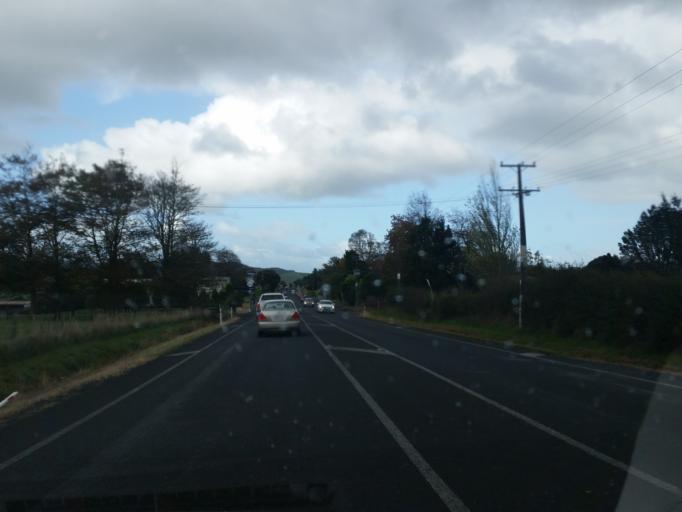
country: NZ
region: Waikato
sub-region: Waikato District
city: Te Kauwhata
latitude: -37.2489
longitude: 175.2199
